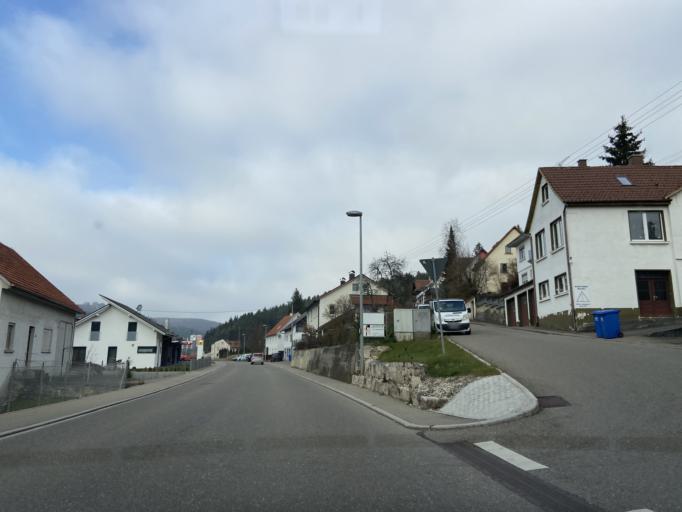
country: DE
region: Baden-Wuerttemberg
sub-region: Tuebingen Region
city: Neufra
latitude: 48.2511
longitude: 9.1820
